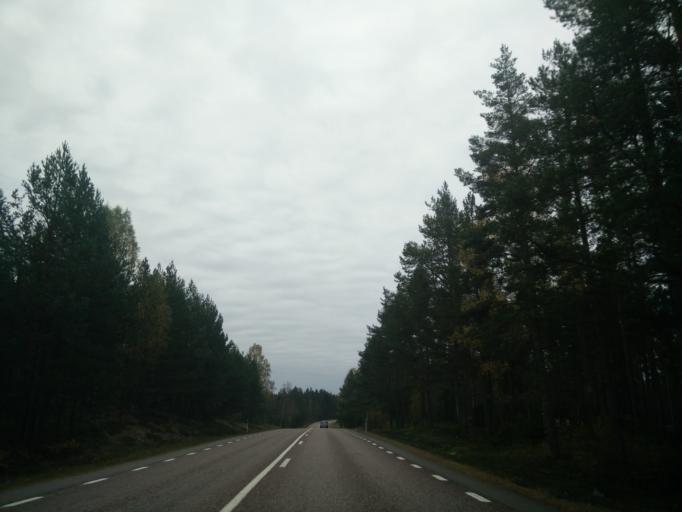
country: SE
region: Gaevleborg
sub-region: Gavle Kommun
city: Norrsundet
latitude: 60.8358
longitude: 17.2041
